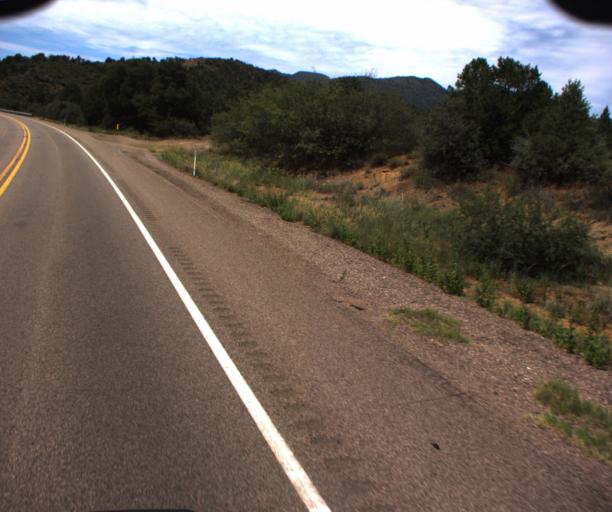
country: US
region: Arizona
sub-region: Gila County
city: Globe
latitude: 33.5640
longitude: -110.6747
